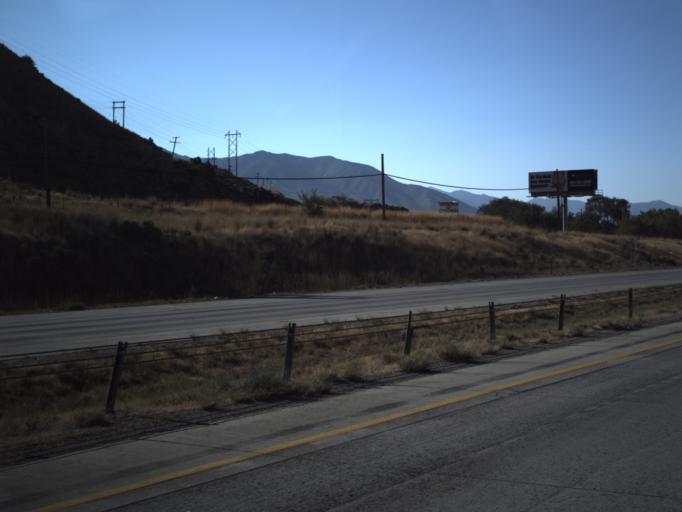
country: US
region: Utah
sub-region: Tooele County
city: Stansbury park
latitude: 40.7040
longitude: -112.2563
